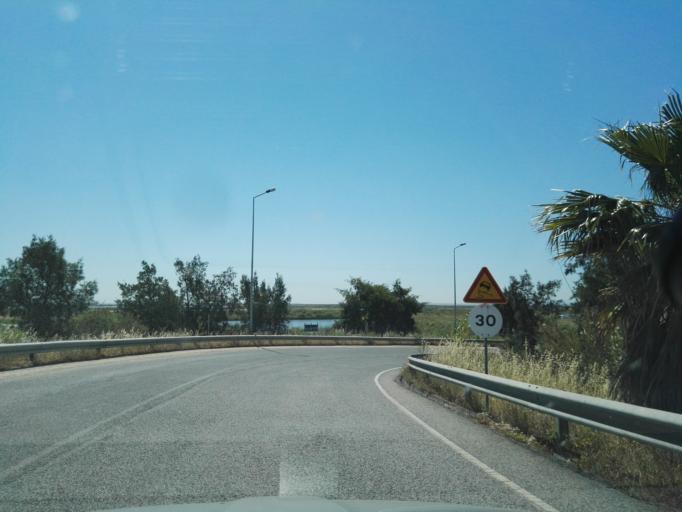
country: PT
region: Lisbon
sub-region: Vila Franca de Xira
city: Sobralinho
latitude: 38.8857
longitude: -9.0377
